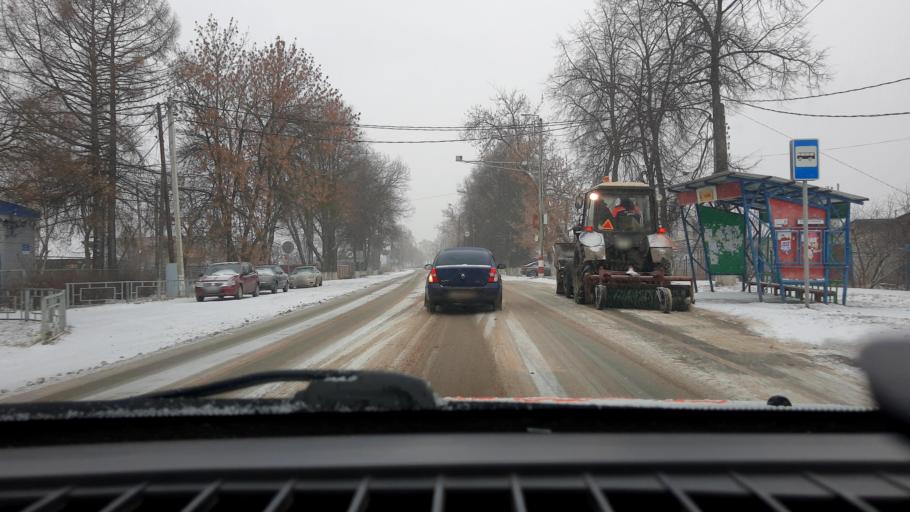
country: RU
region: Nizjnij Novgorod
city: Bor
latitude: 56.3725
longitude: 44.0350
